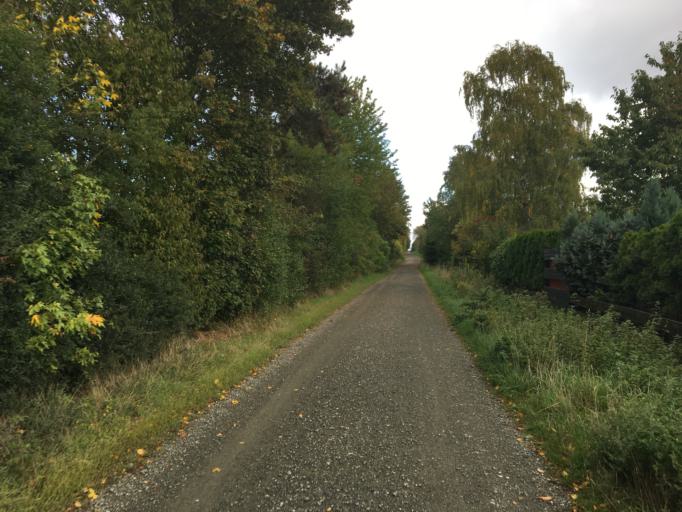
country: DE
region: Lower Saxony
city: Klein Schwulper
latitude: 52.2906
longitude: 10.4570
